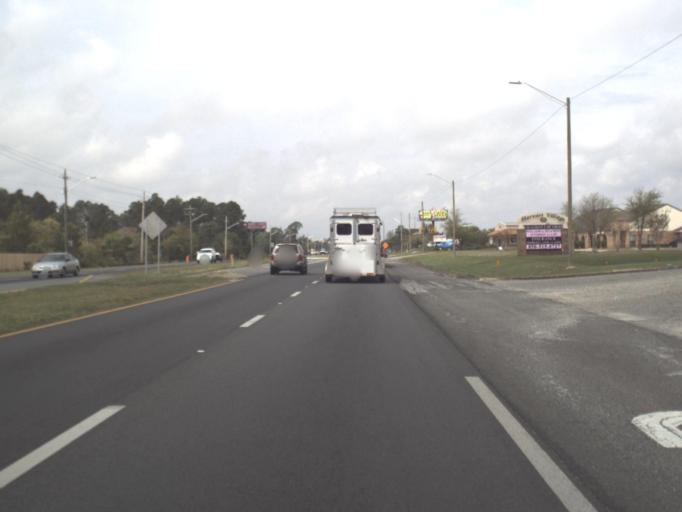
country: US
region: Florida
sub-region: Santa Rosa County
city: Navarre
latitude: 30.4020
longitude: -86.9060
